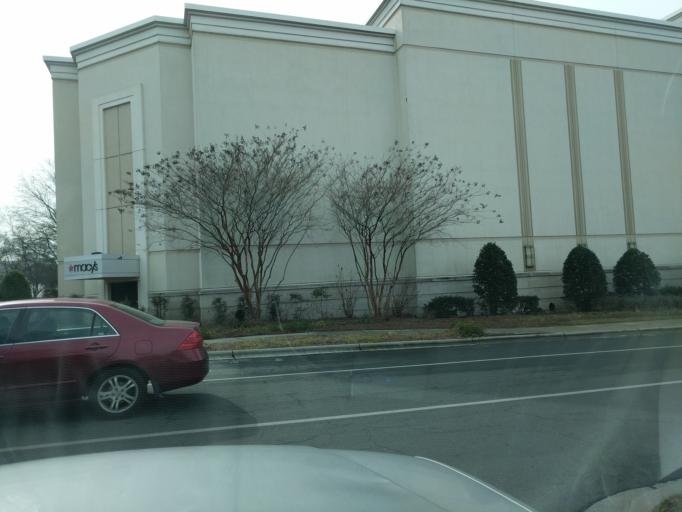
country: US
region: North Carolina
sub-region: Mecklenburg County
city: Charlotte
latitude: 35.1544
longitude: -80.8313
